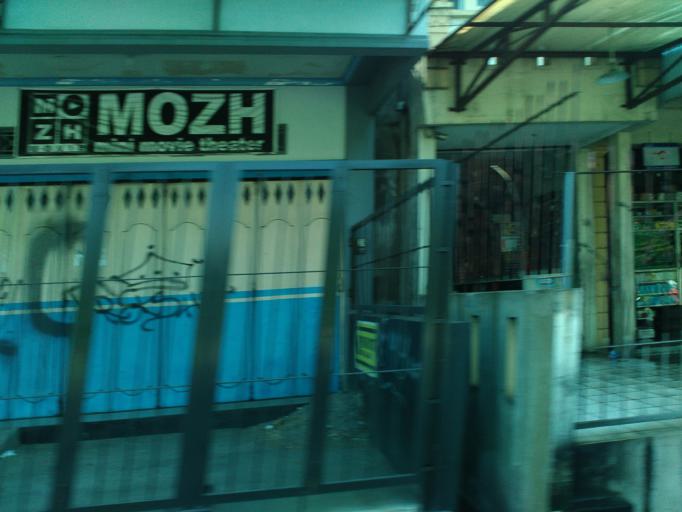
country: ID
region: Central Java
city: Delanggu
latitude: -7.6318
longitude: 110.6937
